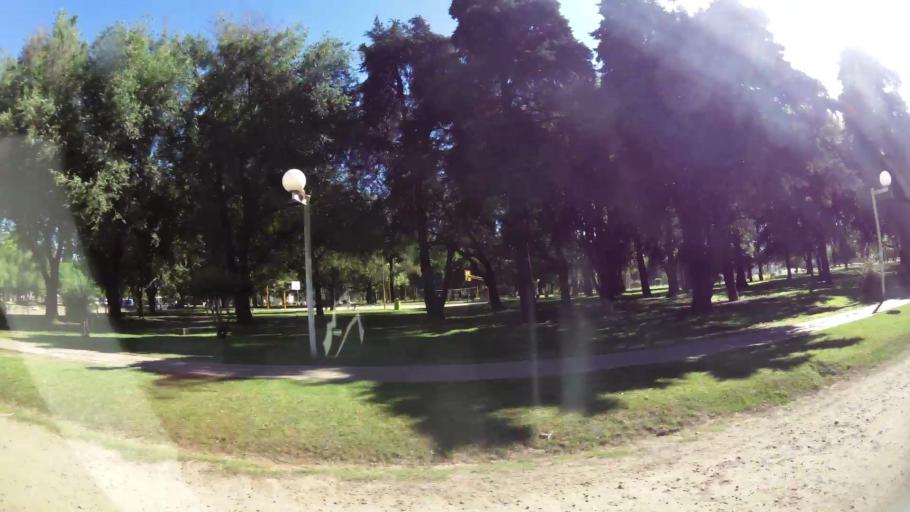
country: AR
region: Santa Fe
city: Esperanza
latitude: -31.4485
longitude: -60.9184
